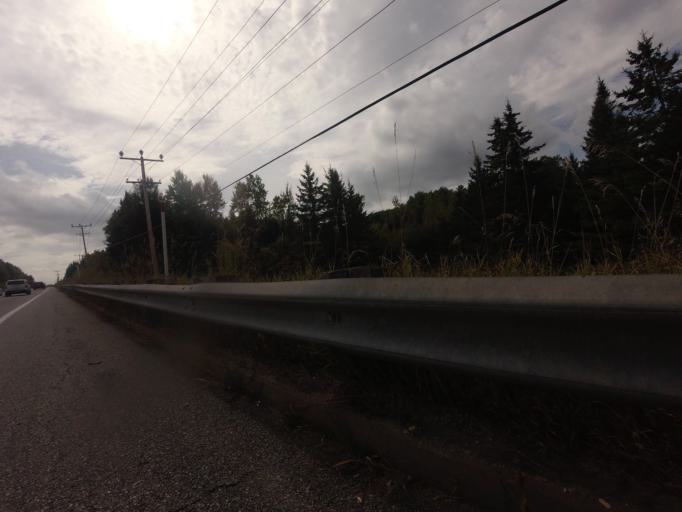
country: CA
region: Quebec
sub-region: Outaouais
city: Wakefield
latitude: 45.8426
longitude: -75.9776
